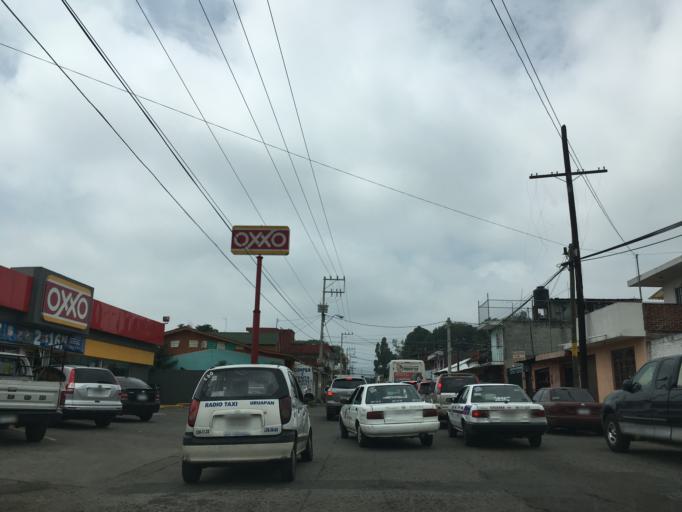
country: MX
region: Michoacan
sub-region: Uruapan
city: Uruapan
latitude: 19.4195
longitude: -102.0465
